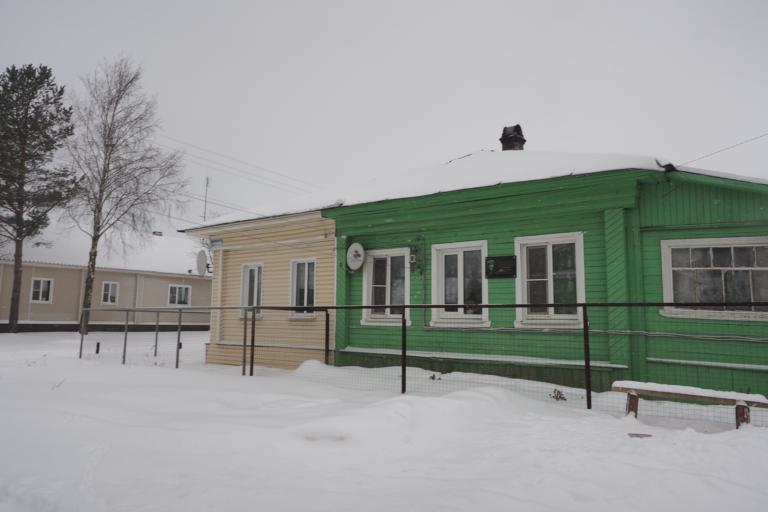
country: RU
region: Tverskaya
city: Ves'yegonsk
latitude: 58.6793
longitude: 37.2541
